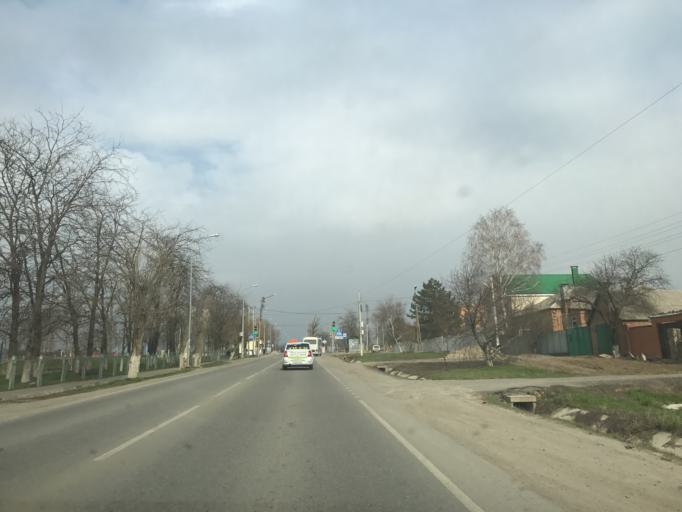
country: RU
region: Rostov
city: Aksay
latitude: 47.2963
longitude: 39.9182
